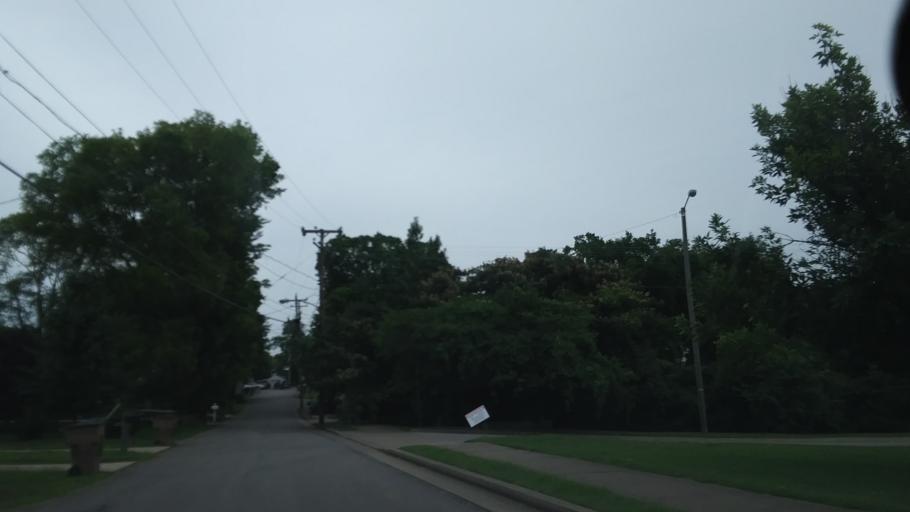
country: US
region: Tennessee
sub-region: Davidson County
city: Belle Meade
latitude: 36.1434
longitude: -86.8561
